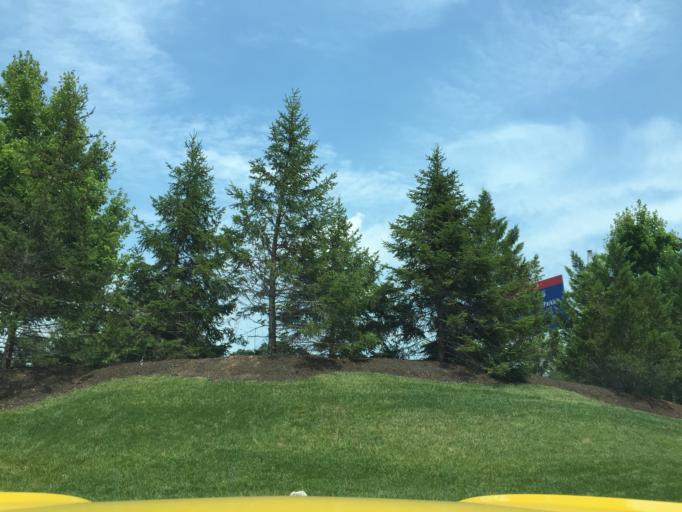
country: US
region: Maryland
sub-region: Prince George's County
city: Forest Heights
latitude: 38.7858
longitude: -77.0147
